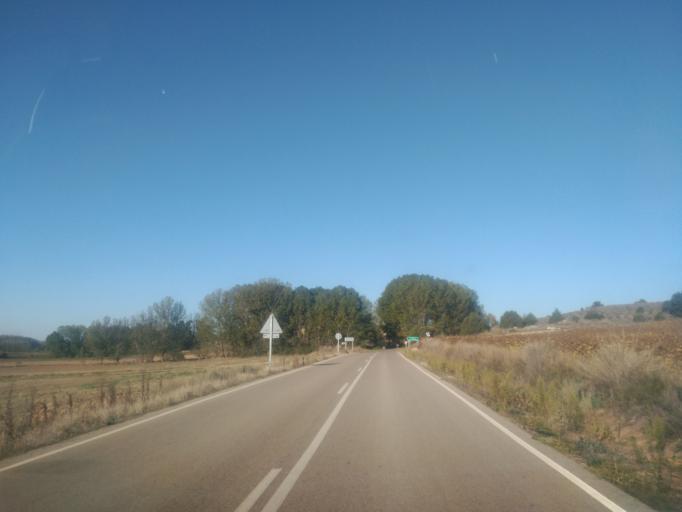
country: ES
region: Castille and Leon
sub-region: Provincia de Burgos
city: Brazacorta
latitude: 41.7188
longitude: -3.3593
